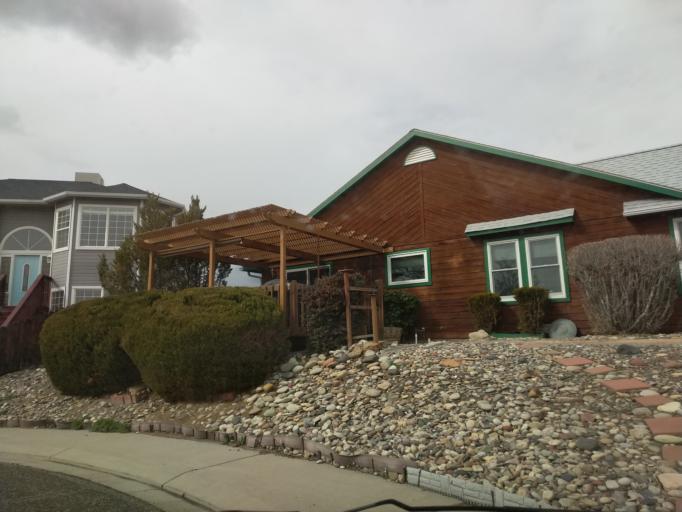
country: US
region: Colorado
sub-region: Mesa County
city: Fruitvale
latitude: 39.0911
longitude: -108.5247
